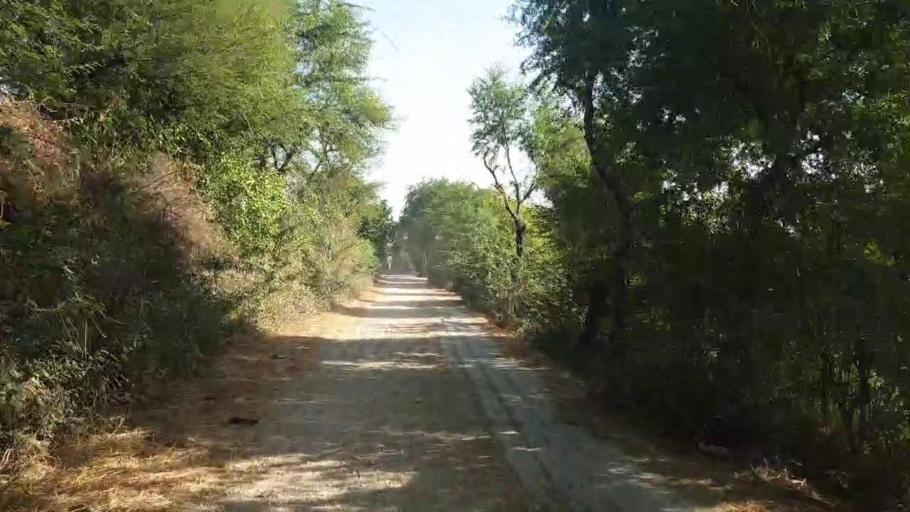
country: PK
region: Sindh
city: Matli
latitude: 25.0274
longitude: 68.7327
